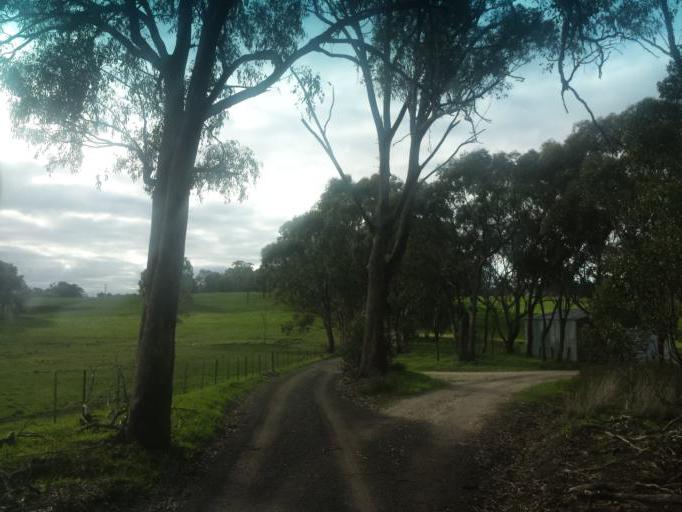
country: AU
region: Victoria
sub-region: Murrindindi
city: Kinglake West
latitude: -37.0292
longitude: 145.2502
